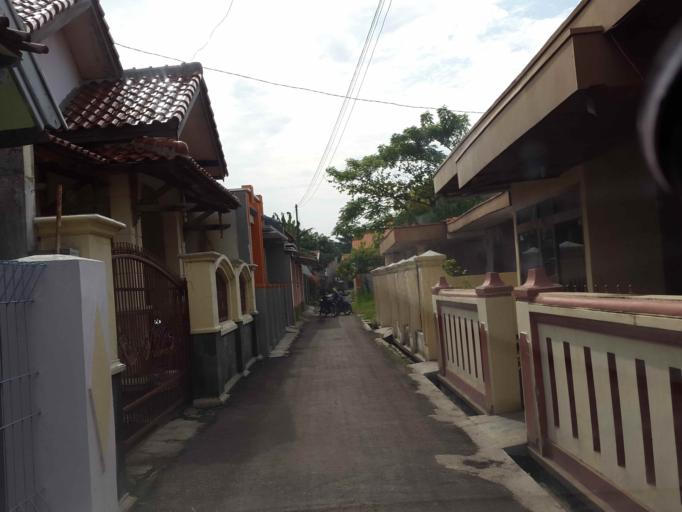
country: ID
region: Central Java
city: Dukuhturi
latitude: -6.8736
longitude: 109.0542
